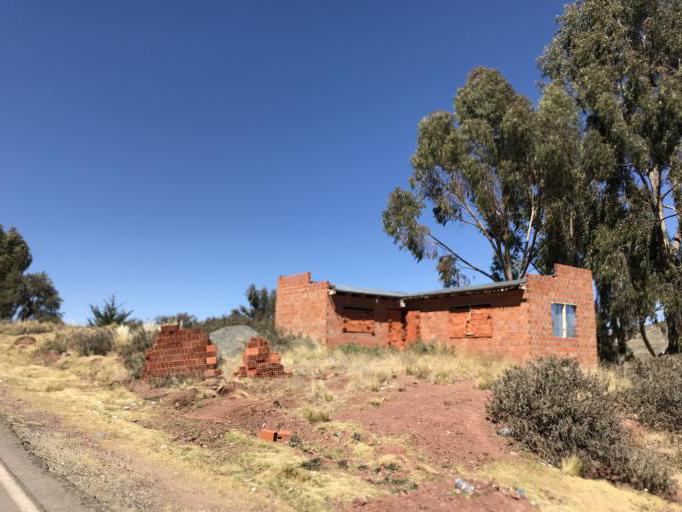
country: BO
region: La Paz
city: San Pablo
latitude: -16.2162
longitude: -68.8439
